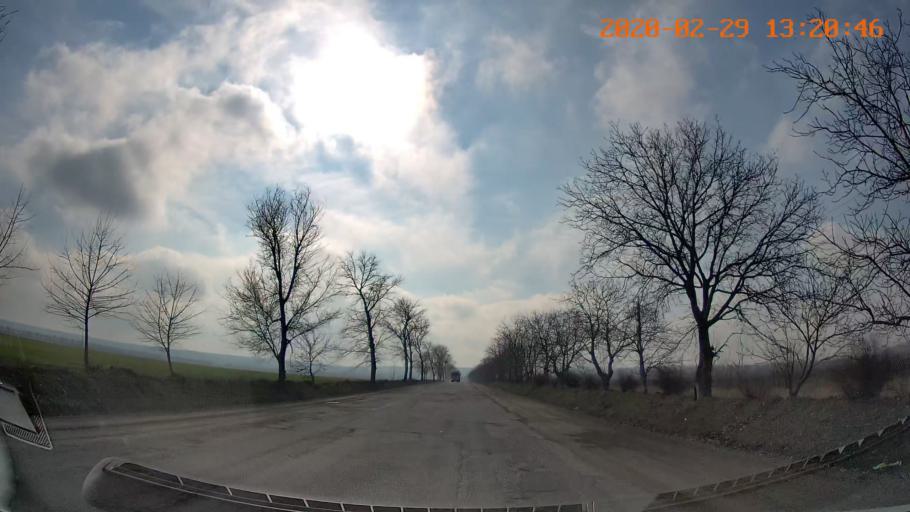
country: MD
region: Telenesti
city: Camenca
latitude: 47.9759
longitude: 28.6385
